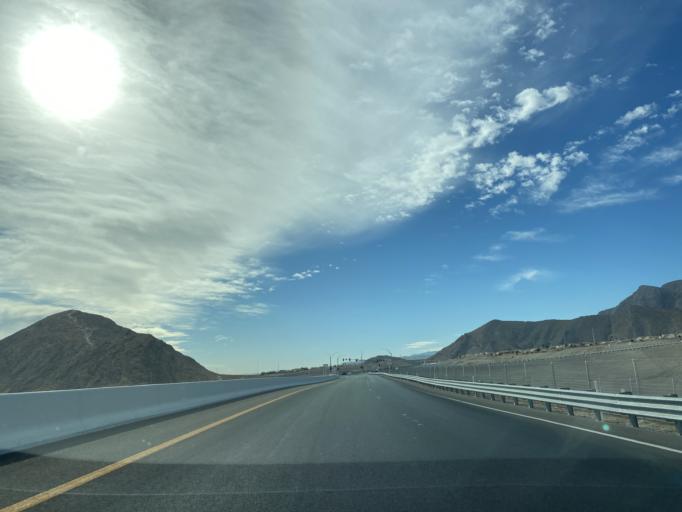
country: US
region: Nevada
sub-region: Clark County
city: Summerlin South
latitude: 36.2505
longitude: -115.3181
